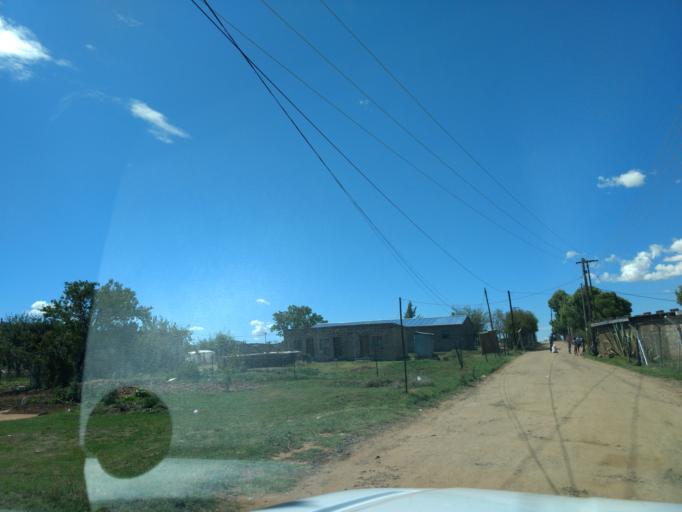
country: LS
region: Maseru
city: Maseru
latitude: -29.3697
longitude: 27.5119
